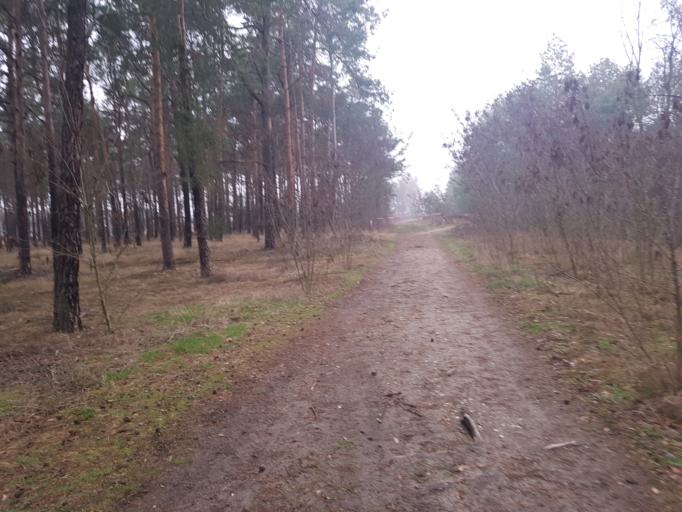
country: DE
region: Brandenburg
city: Schonewalde
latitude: 51.6347
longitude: 13.6208
